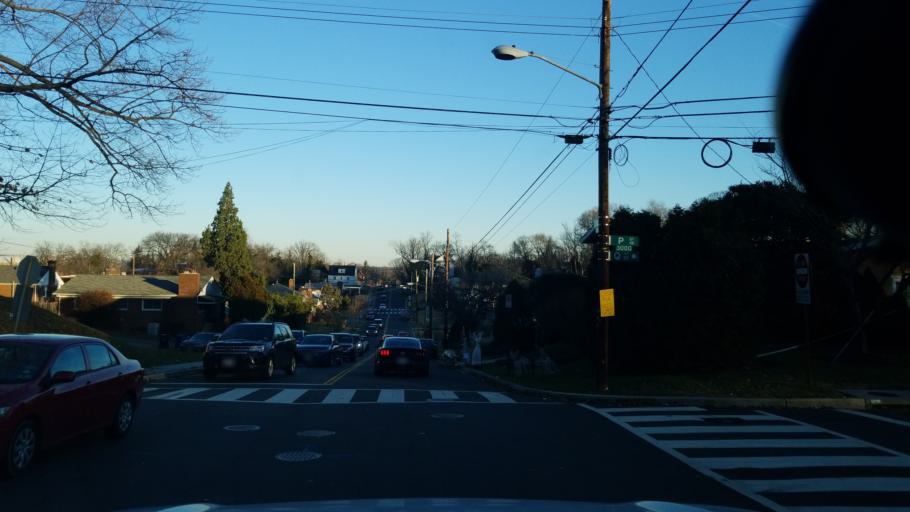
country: US
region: Maryland
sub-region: Prince George's County
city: Silver Hill
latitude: 38.8719
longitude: -76.9647
